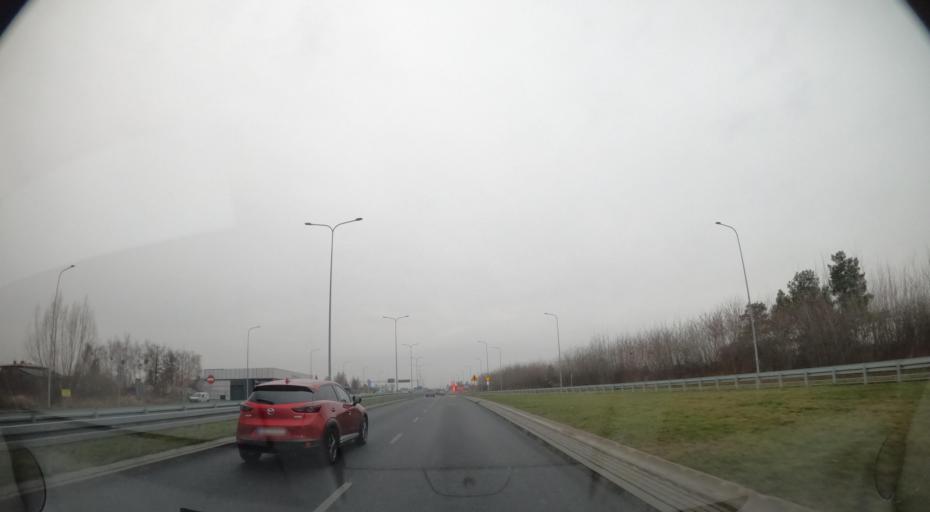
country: PL
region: Masovian Voivodeship
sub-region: Radom
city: Radom
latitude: 51.3953
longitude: 21.1962
